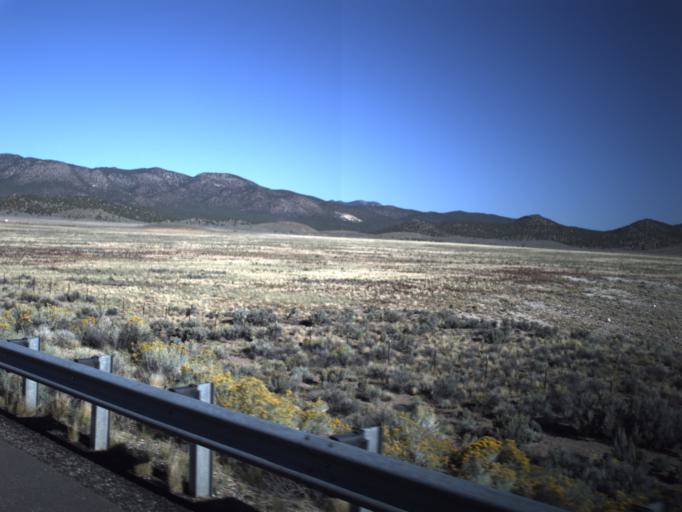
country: US
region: Utah
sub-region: Washington County
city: Enterprise
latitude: 37.8023
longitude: -113.9188
